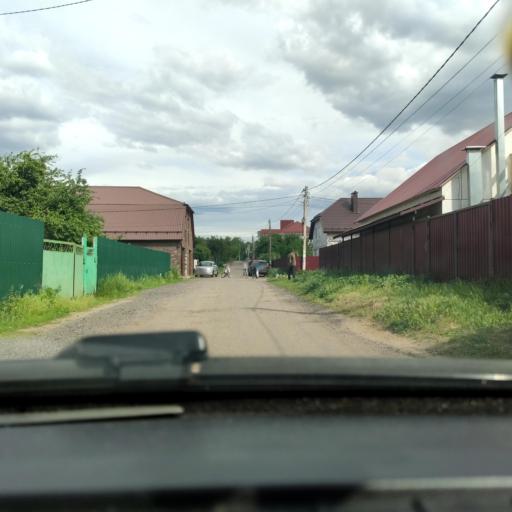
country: RU
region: Voronezj
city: Pridonskoy
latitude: 51.6390
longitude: 39.0823
